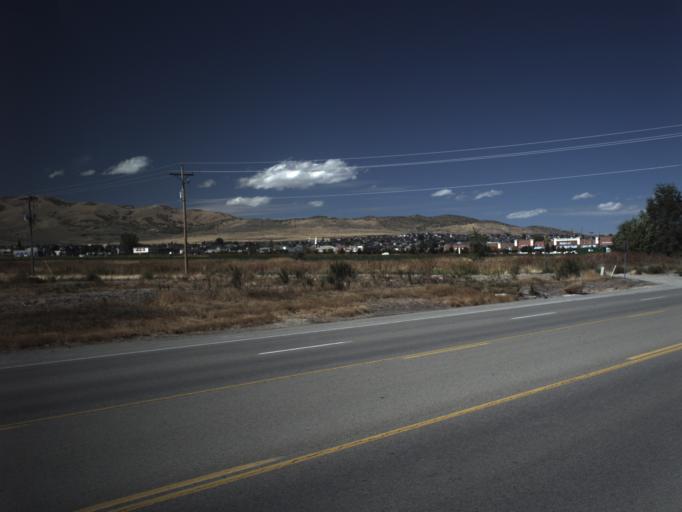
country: US
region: Utah
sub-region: Utah County
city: Saratoga Springs
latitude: 40.3833
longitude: -111.9163
